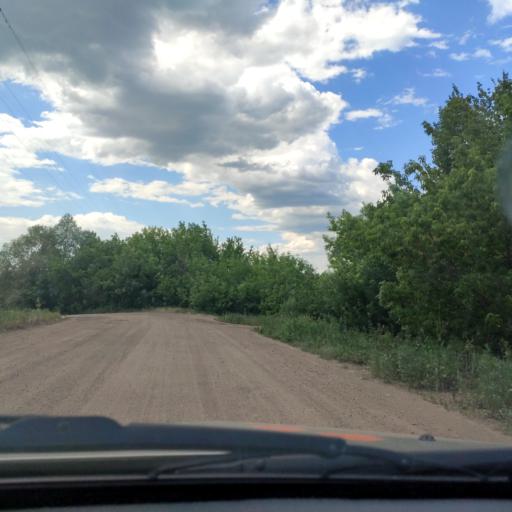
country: RU
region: Bashkortostan
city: Ufa
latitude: 54.8344
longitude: 56.0626
